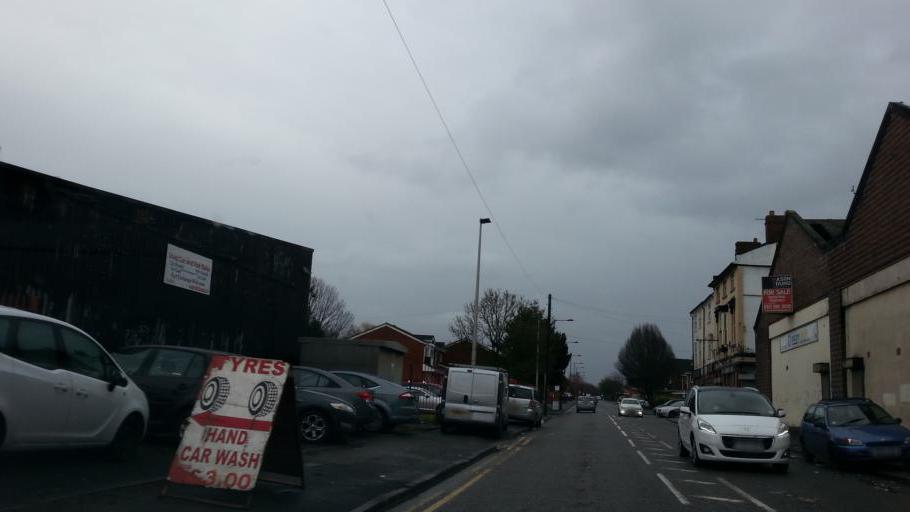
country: GB
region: England
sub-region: City and Borough of Birmingham
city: Hockley
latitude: 52.4912
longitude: -1.9445
